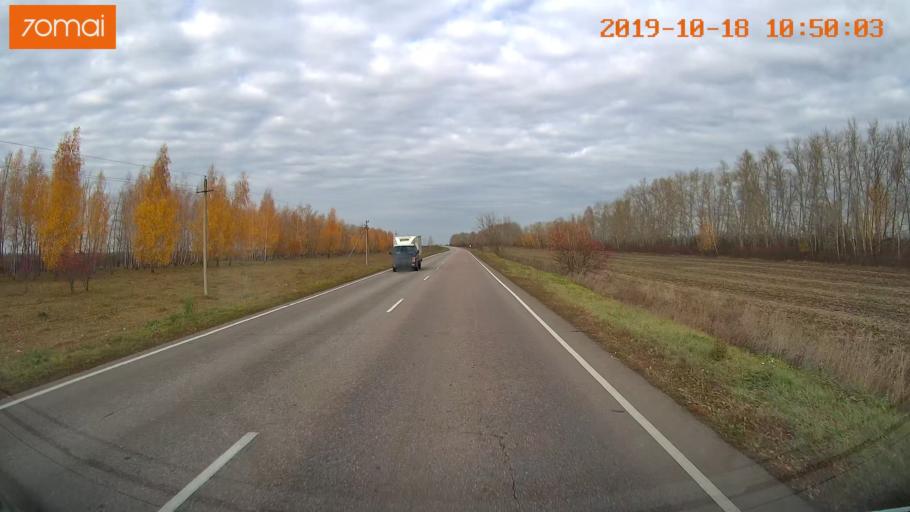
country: RU
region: Tula
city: Yepifan'
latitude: 53.7399
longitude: 38.6874
